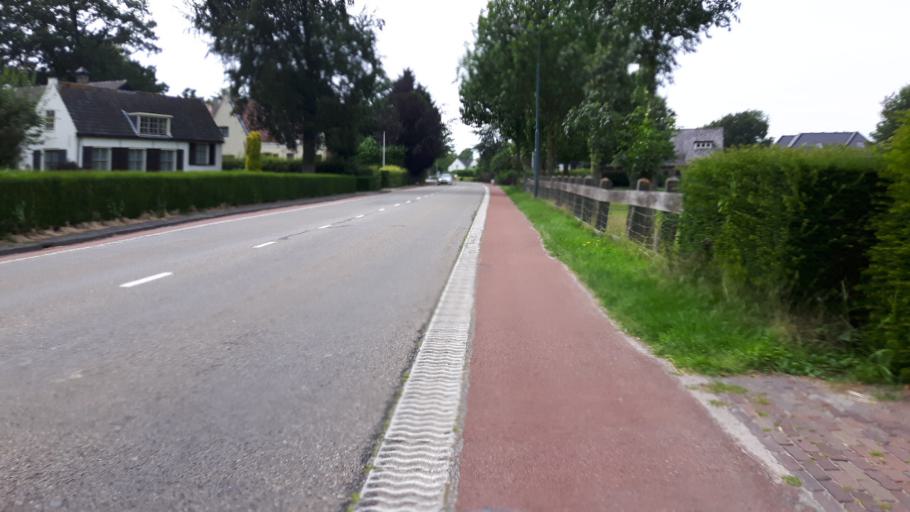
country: NL
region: North Holland
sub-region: Gemeente Wijdemeren
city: Nieuw-Loosdrecht
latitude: 52.2061
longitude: 5.1249
